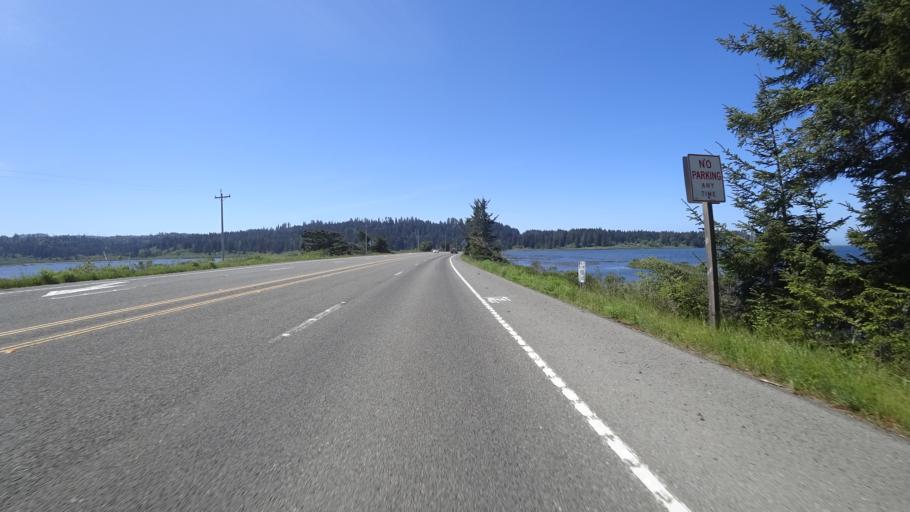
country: US
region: California
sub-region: Humboldt County
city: Westhaven-Moonstone
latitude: 41.1650
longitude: -124.1065
